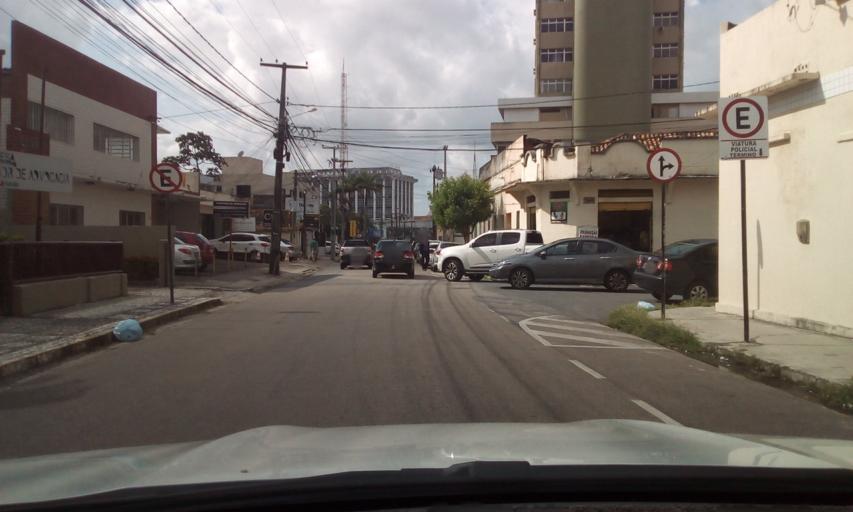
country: BR
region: Paraiba
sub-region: Joao Pessoa
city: Joao Pessoa
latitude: -7.1252
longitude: -34.8831
